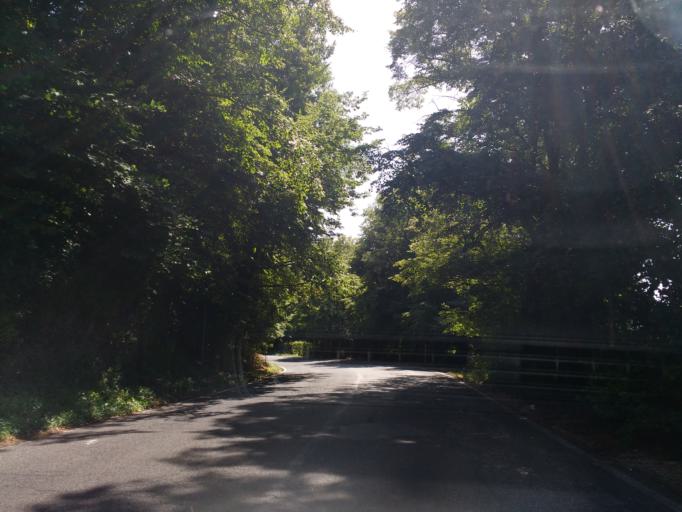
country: IT
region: Latium
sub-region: Citta metropolitana di Roma Capitale
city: Rocca di Papa
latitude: 41.7533
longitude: 12.7012
